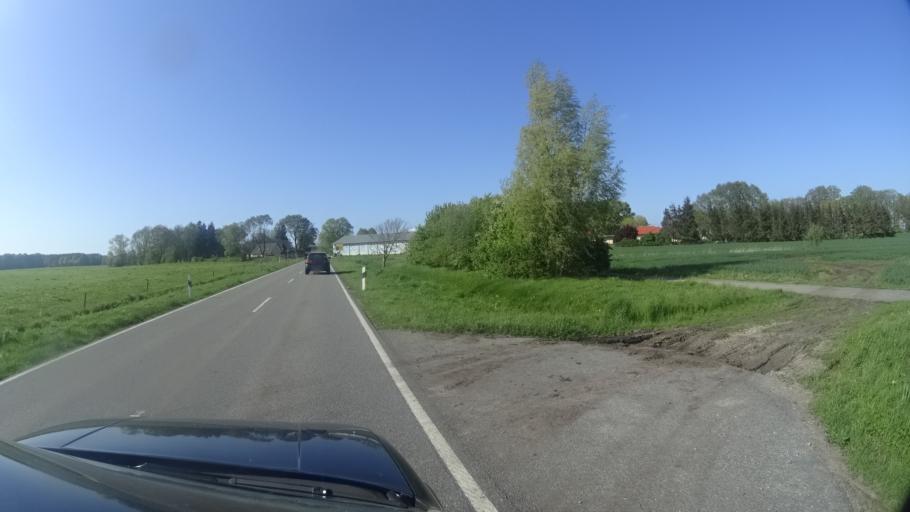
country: DE
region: Mecklenburg-Vorpommern
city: Ostseebad Dierhagen
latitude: 54.2578
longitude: 12.3553
